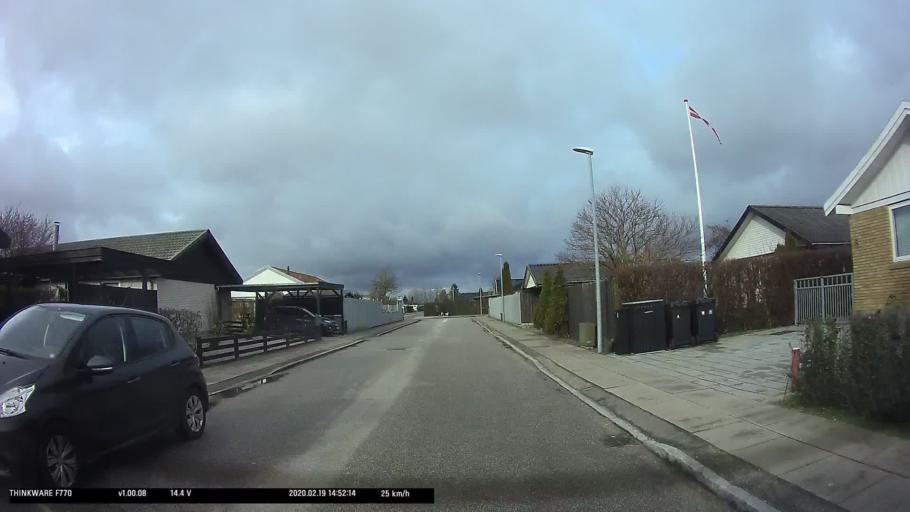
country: DK
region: Capital Region
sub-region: Tarnby Kommune
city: Tarnby
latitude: 55.5896
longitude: 12.5763
